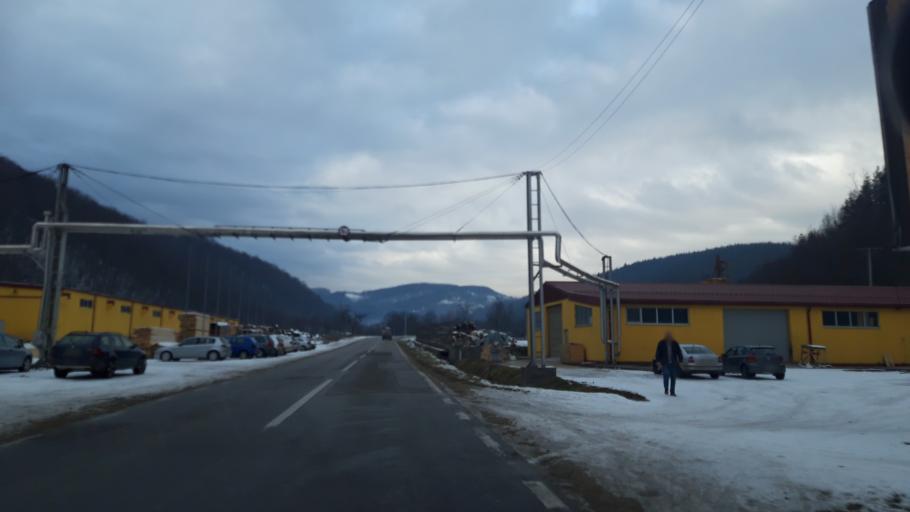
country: BA
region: Republika Srpska
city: Milici
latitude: 44.1659
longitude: 19.0380
